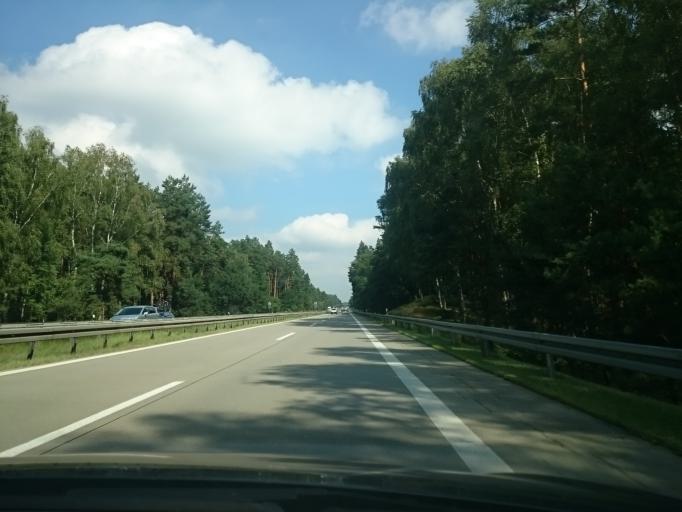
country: DE
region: Brandenburg
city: Marienwerder
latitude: 52.8002
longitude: 13.6085
